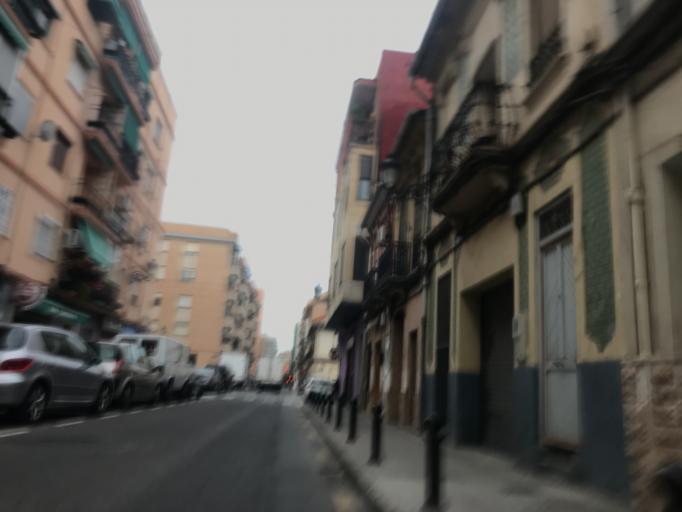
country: ES
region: Valencia
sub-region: Provincia de Valencia
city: Valencia
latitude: 39.4657
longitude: -0.3444
